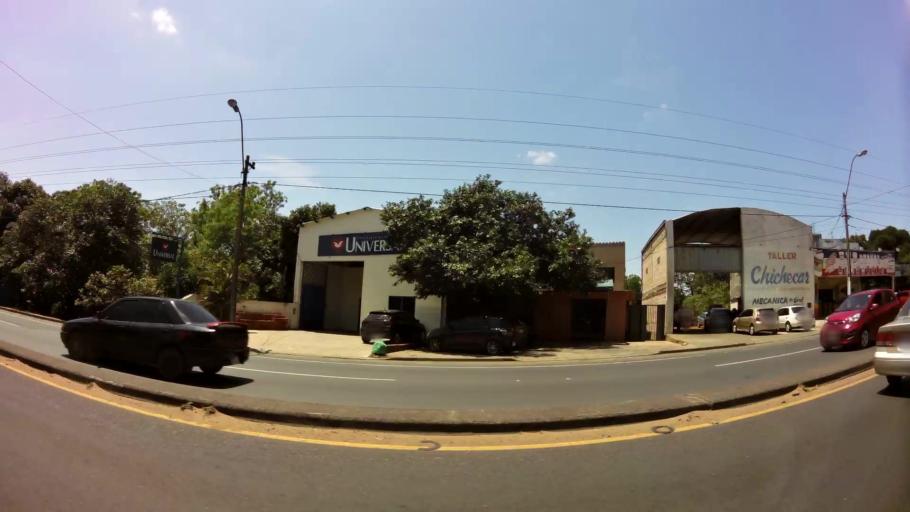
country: PY
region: Central
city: Nemby
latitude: -25.3996
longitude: -57.5434
